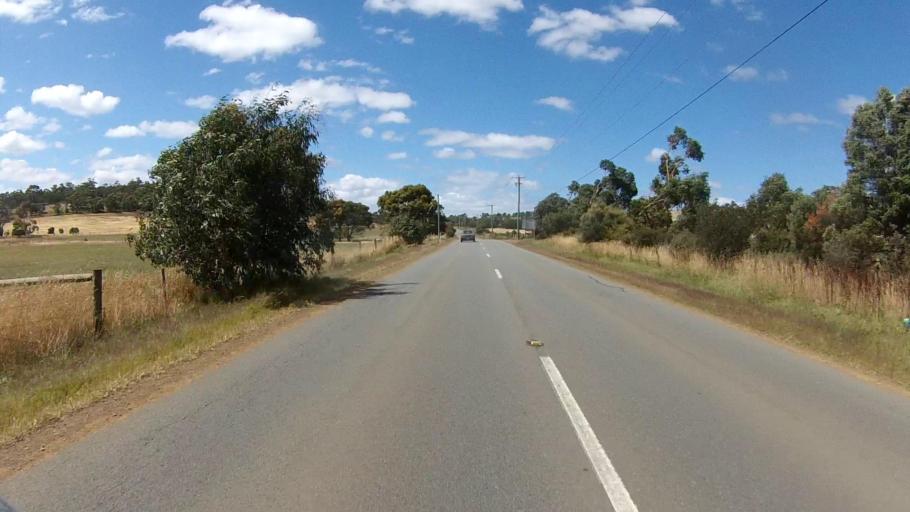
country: AU
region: Tasmania
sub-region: Clarence
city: Cambridge
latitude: -42.8169
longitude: 147.4364
